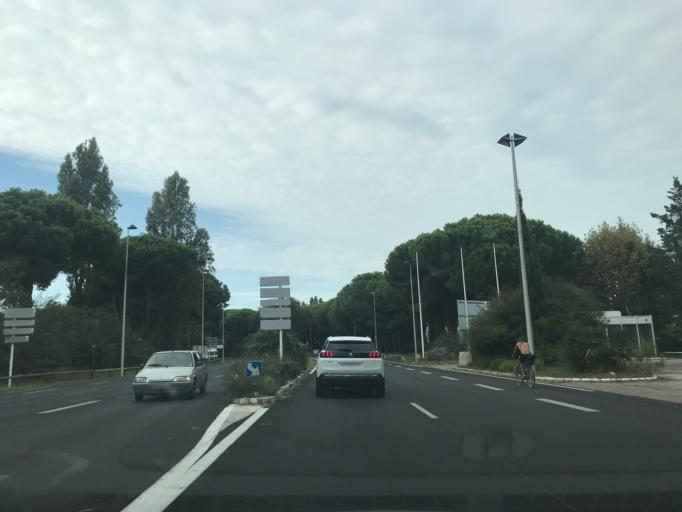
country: FR
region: Languedoc-Roussillon
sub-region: Departement de l'Herault
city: La Grande-Motte
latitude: 43.5617
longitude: 4.0962
